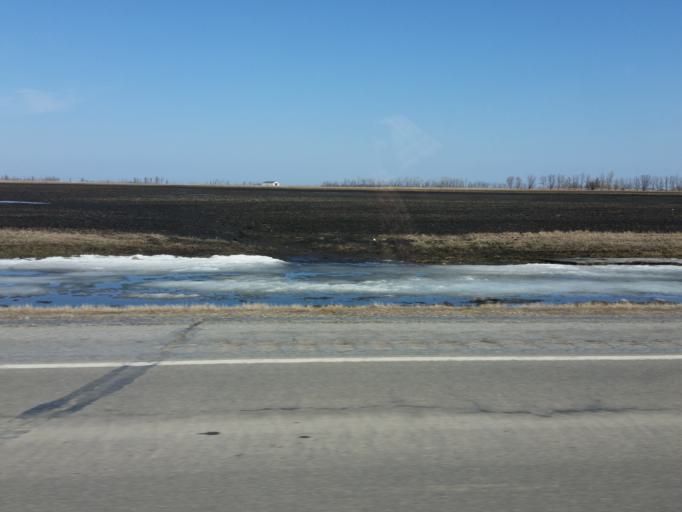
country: US
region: North Dakota
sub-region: Walsh County
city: Grafton
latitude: 48.2981
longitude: -97.3759
